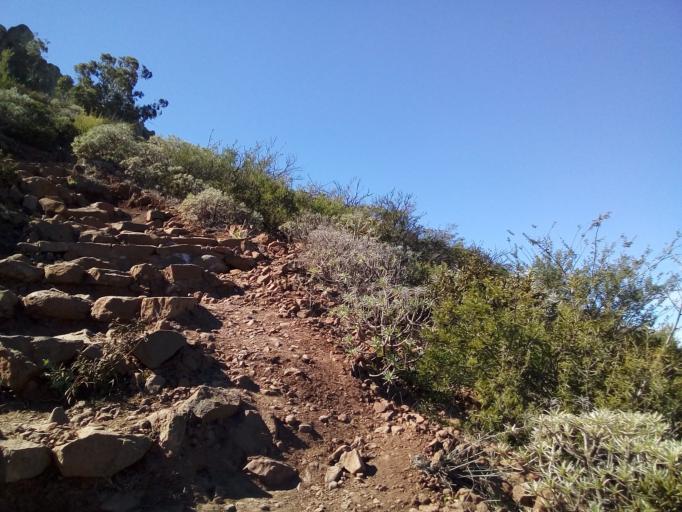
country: ES
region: Canary Islands
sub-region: Provincia de Santa Cruz de Tenerife
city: Alajero
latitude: 28.1020
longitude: -17.2744
